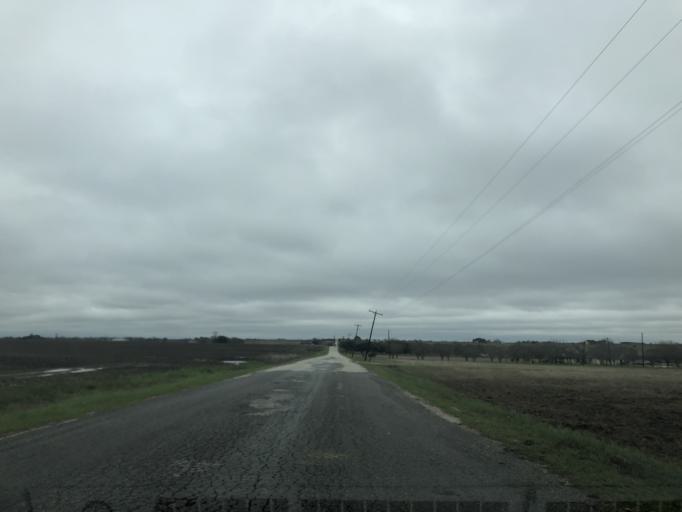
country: US
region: Texas
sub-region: Williamson County
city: Hutto
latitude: 30.5956
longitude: -97.5025
